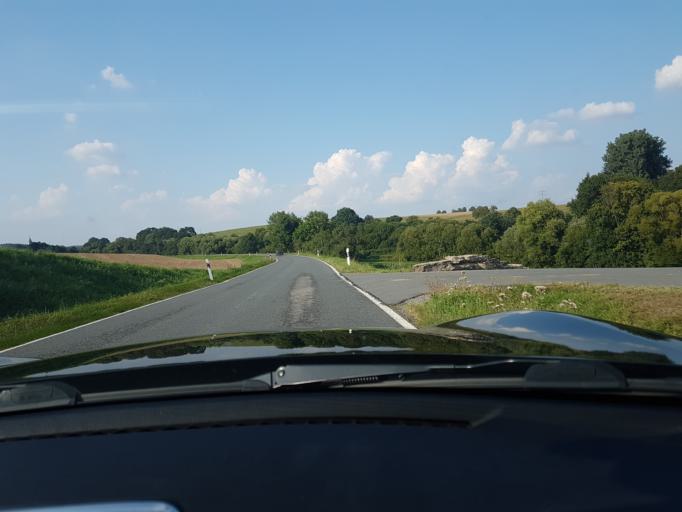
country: DE
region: Baden-Wuerttemberg
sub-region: Karlsruhe Region
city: Seckach
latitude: 49.4436
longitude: 9.3703
